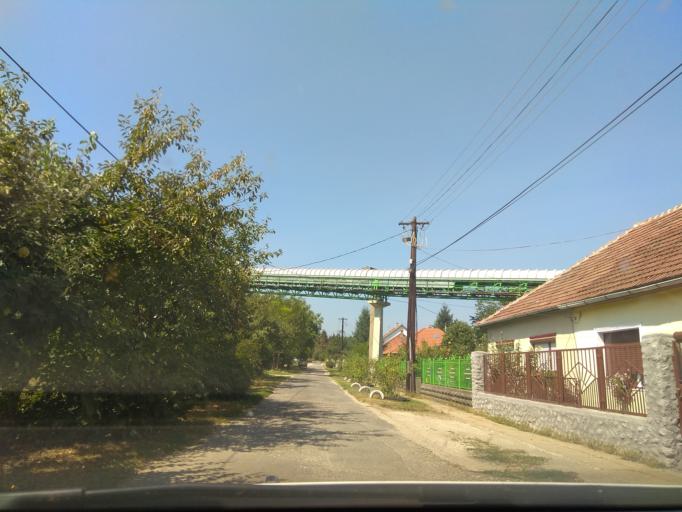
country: HU
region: Borsod-Abauj-Zemplen
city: Miskolc
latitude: 48.0649
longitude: 20.7789
